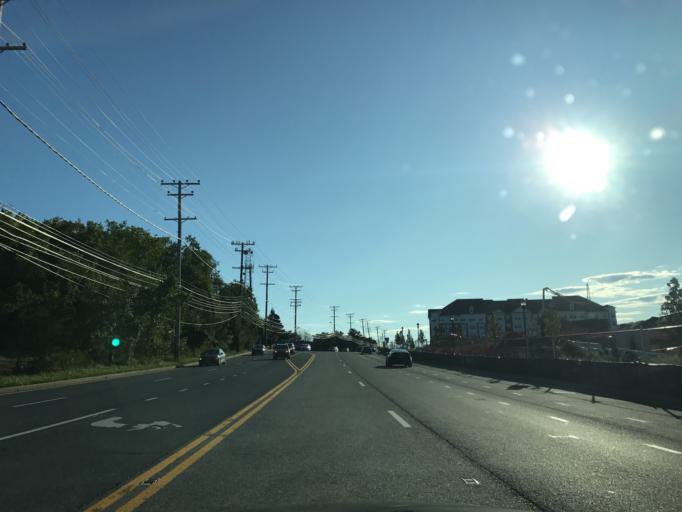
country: US
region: Maryland
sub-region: Anne Arundel County
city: Jessup
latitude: 39.1744
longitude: -76.7792
